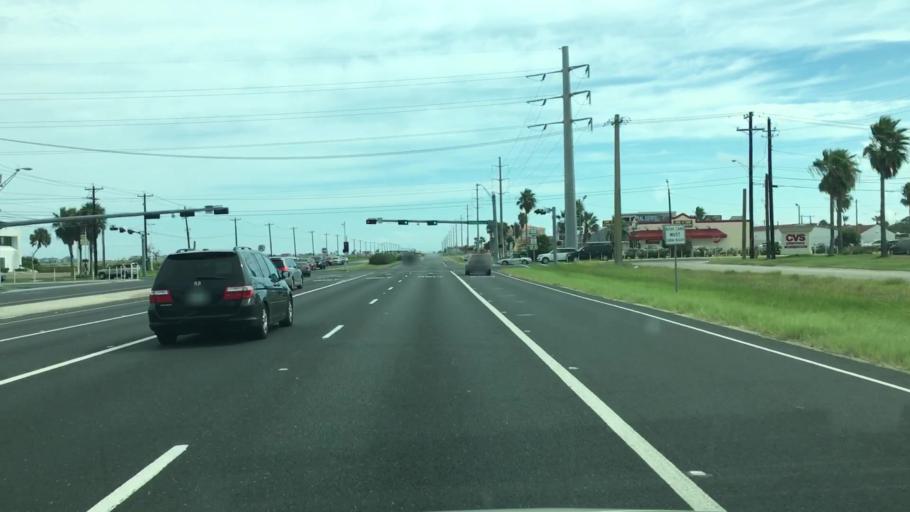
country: US
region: Texas
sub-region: Nueces County
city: Corpus Christi
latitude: 27.6188
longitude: -97.2219
